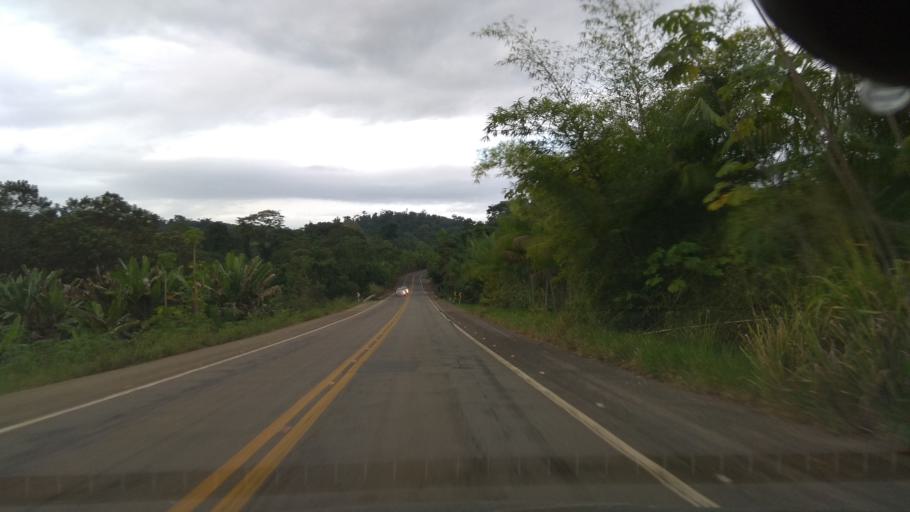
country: BR
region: Bahia
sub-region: Ubata
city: Ubata
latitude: -14.2291
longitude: -39.4421
